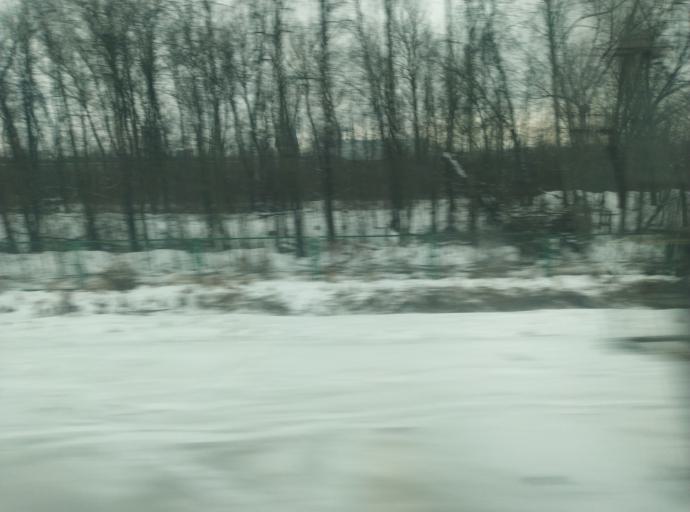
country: RU
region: St.-Petersburg
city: Obukhovo
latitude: 59.8374
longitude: 30.4705
